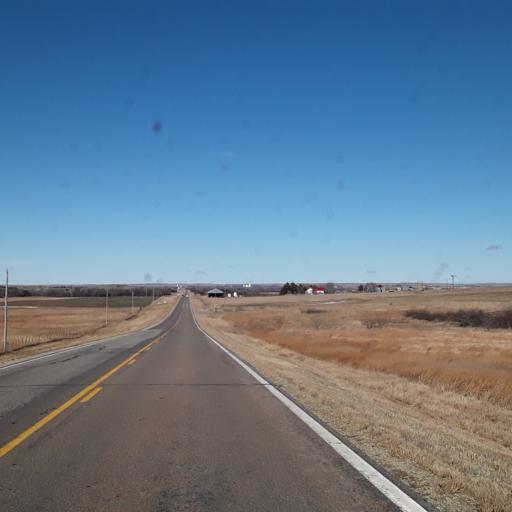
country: US
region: Kansas
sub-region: Lincoln County
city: Lincoln
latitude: 38.9611
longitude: -98.1512
